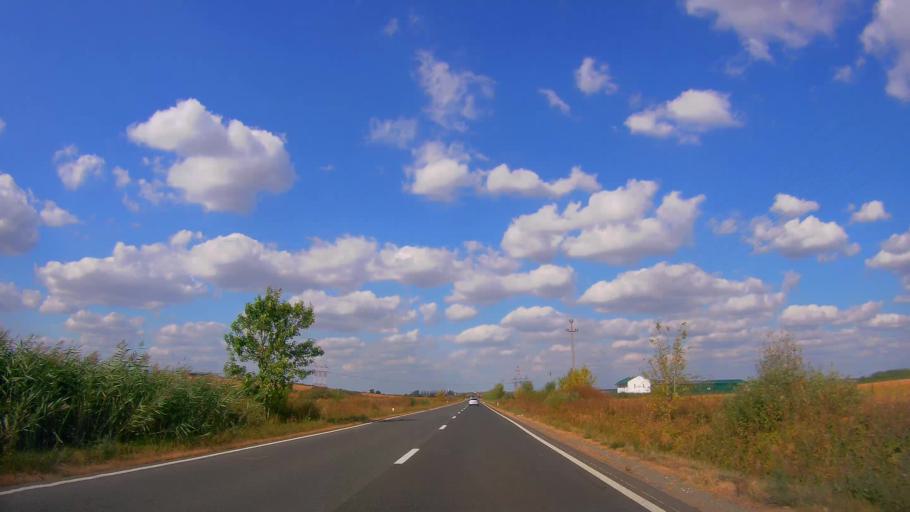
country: RO
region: Satu Mare
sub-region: Oras Ardud
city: Ardud
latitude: 47.6026
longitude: 22.8790
